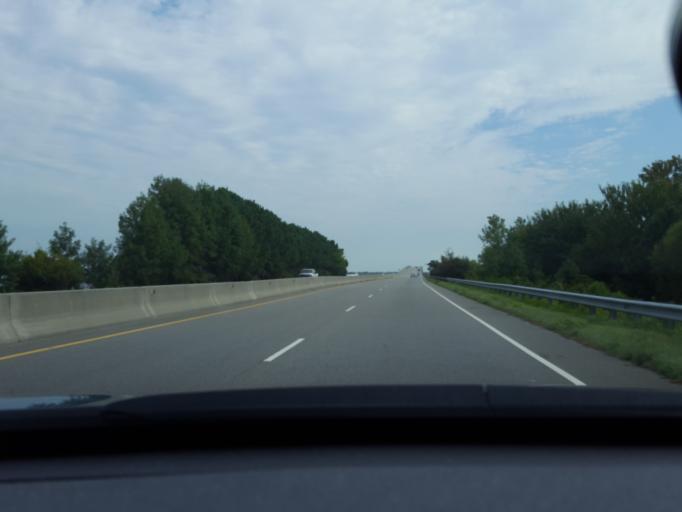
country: US
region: North Carolina
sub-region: Chowan County
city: Edenton
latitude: 36.0414
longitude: -76.7082
